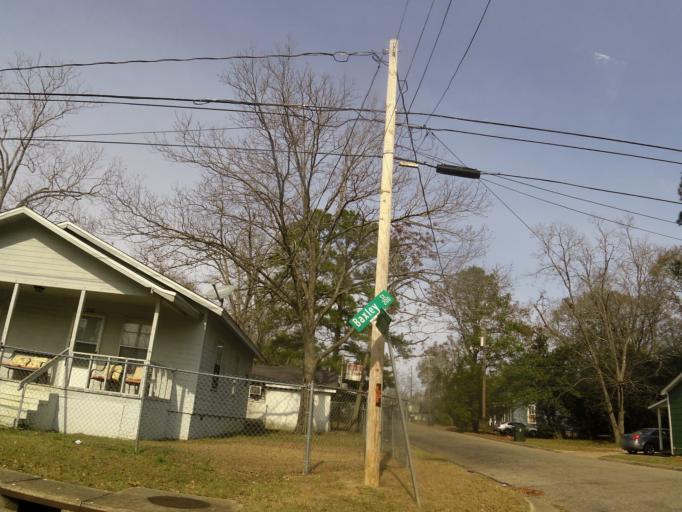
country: US
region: Alabama
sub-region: Houston County
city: Dothan
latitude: 31.2366
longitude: -85.3937
